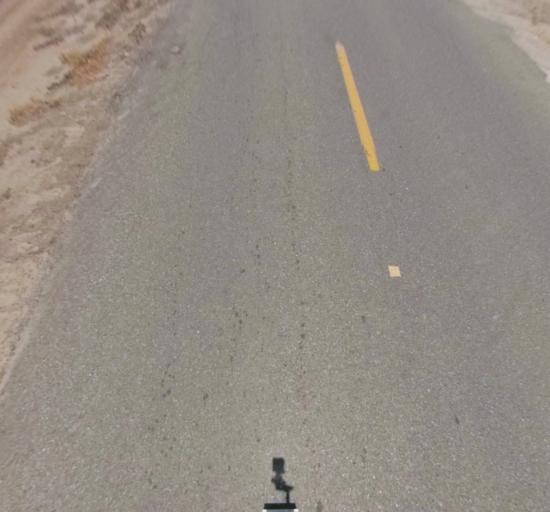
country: US
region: California
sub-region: Madera County
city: Chowchilla
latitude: 37.0952
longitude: -120.2746
